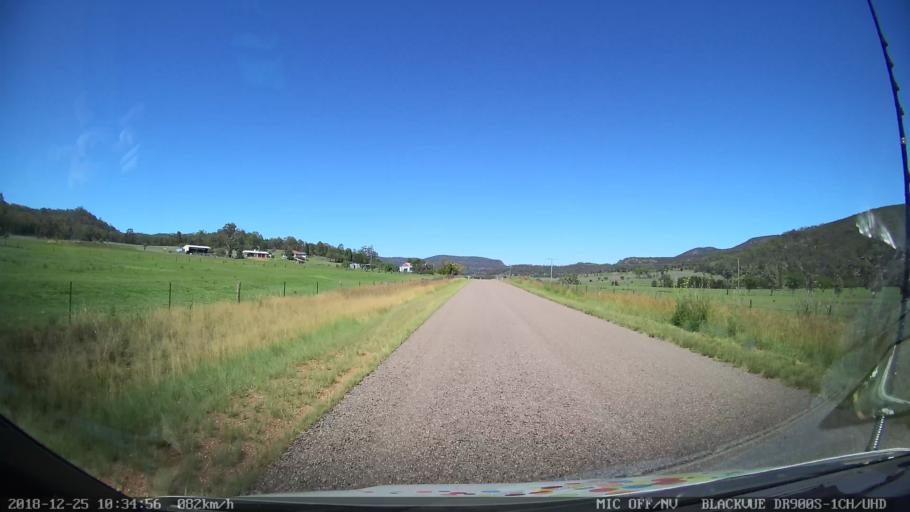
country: AU
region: New South Wales
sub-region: Upper Hunter Shire
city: Merriwa
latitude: -32.3948
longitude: 150.4015
